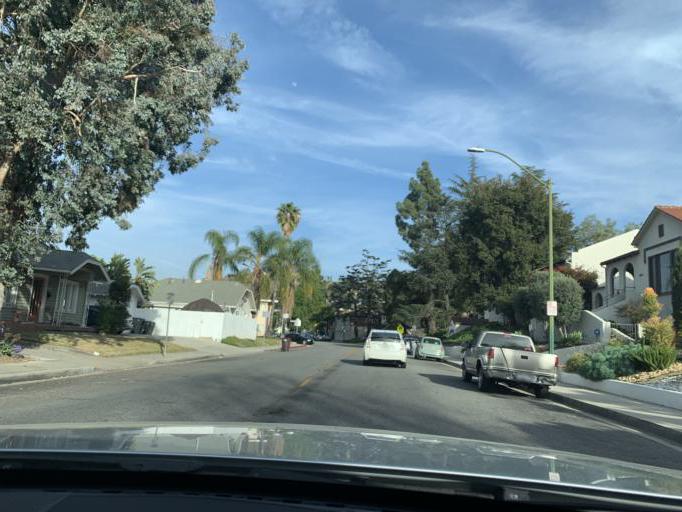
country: US
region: California
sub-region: Los Angeles County
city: Glendale
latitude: 34.1356
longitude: -118.2366
